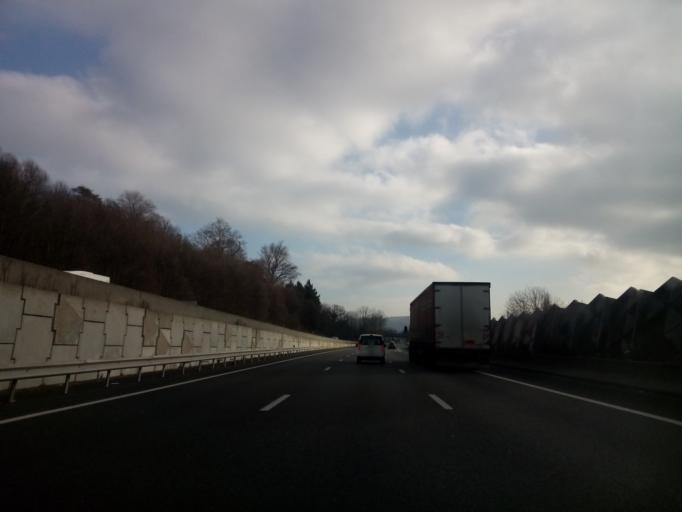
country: FR
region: Rhone-Alpes
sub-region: Departement de l'Isere
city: Bourgoin
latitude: 45.5941
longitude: 5.2885
